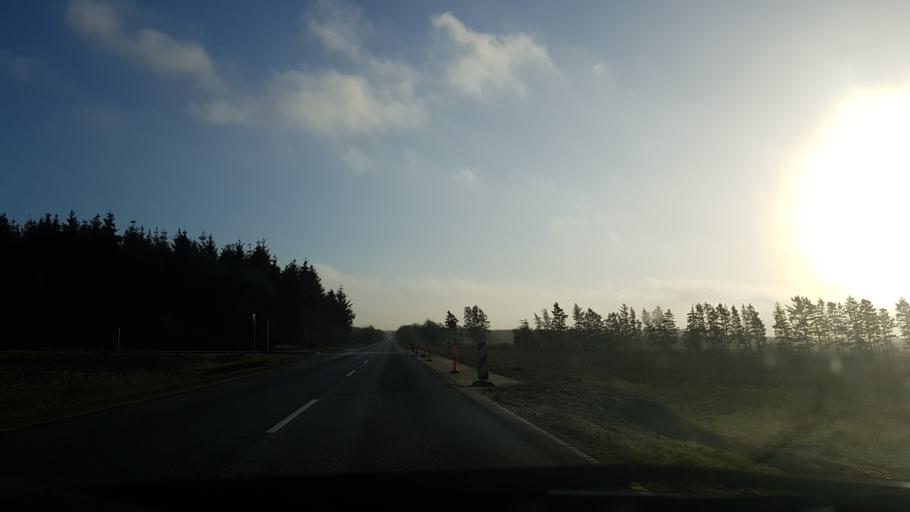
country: DK
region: South Denmark
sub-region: Tonder Kommune
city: Toftlund
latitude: 55.2122
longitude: 9.1867
